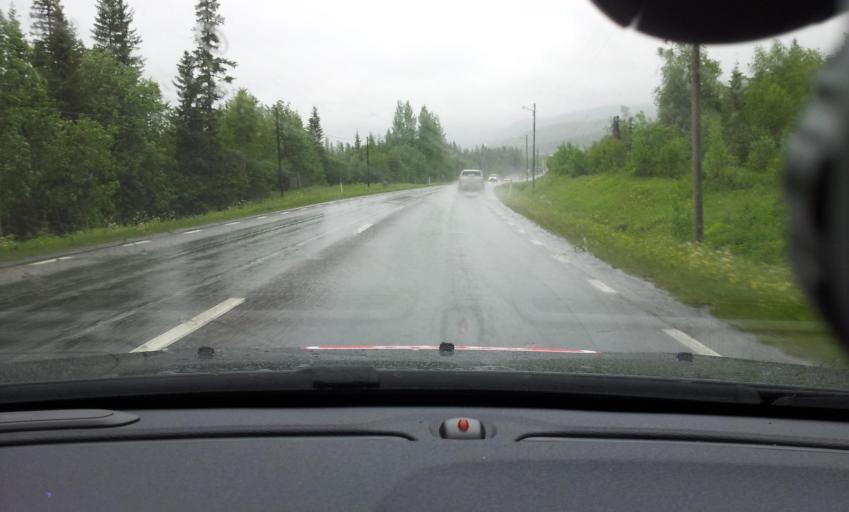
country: SE
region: Jaemtland
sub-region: Are Kommun
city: Are
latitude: 63.3456
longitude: 13.1924
